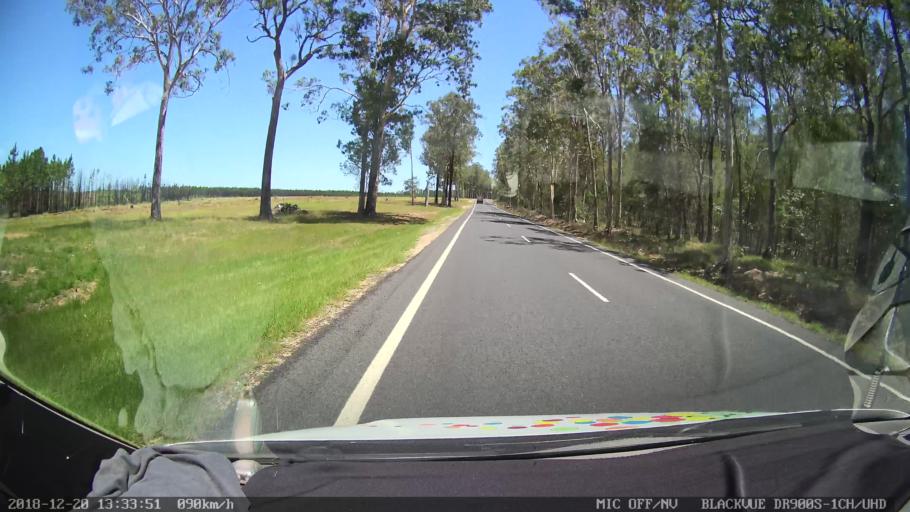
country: AU
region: New South Wales
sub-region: Clarence Valley
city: Gordon
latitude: -29.2510
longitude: 152.9851
